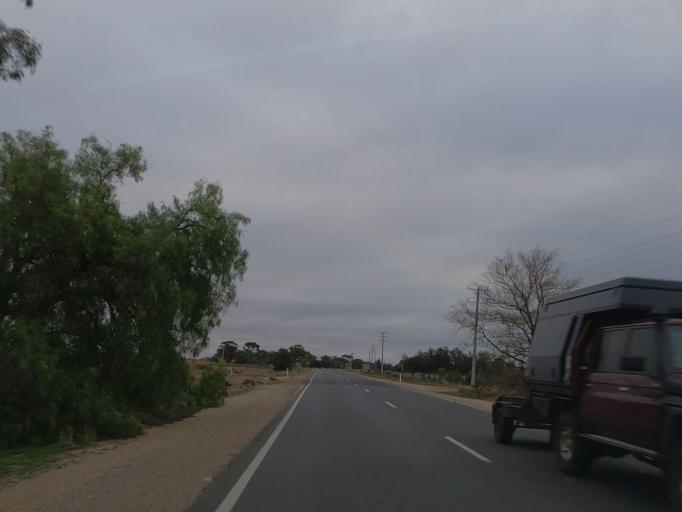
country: AU
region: Victoria
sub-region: Swan Hill
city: Swan Hill
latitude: -35.4435
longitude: 143.6173
